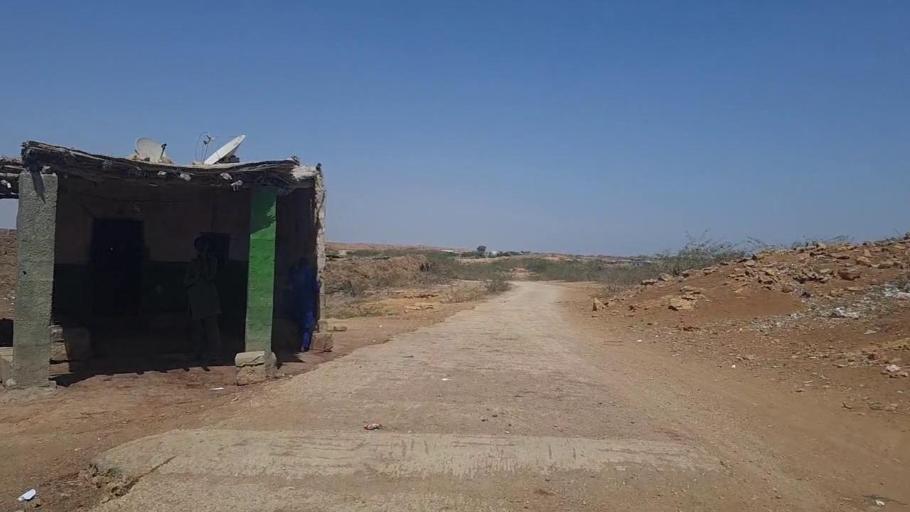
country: PK
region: Sindh
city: Thatta
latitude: 24.8127
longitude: 68.0059
